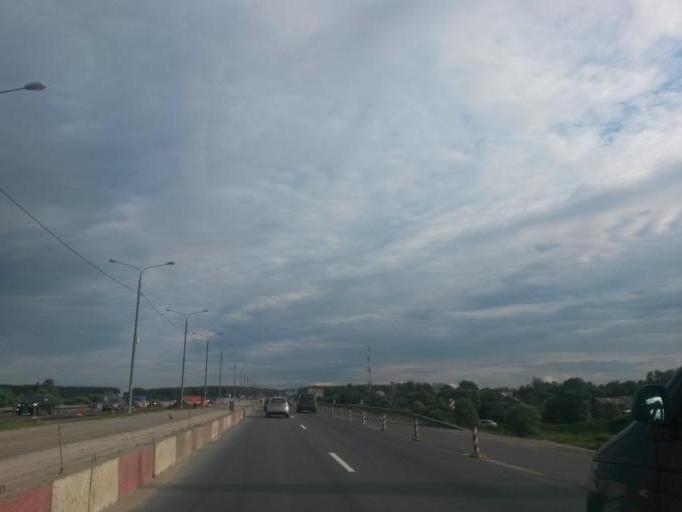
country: RU
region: Moskovskaya
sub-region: Podol'skiy Rayon
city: Podol'sk
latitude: 55.3841
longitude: 37.6046
